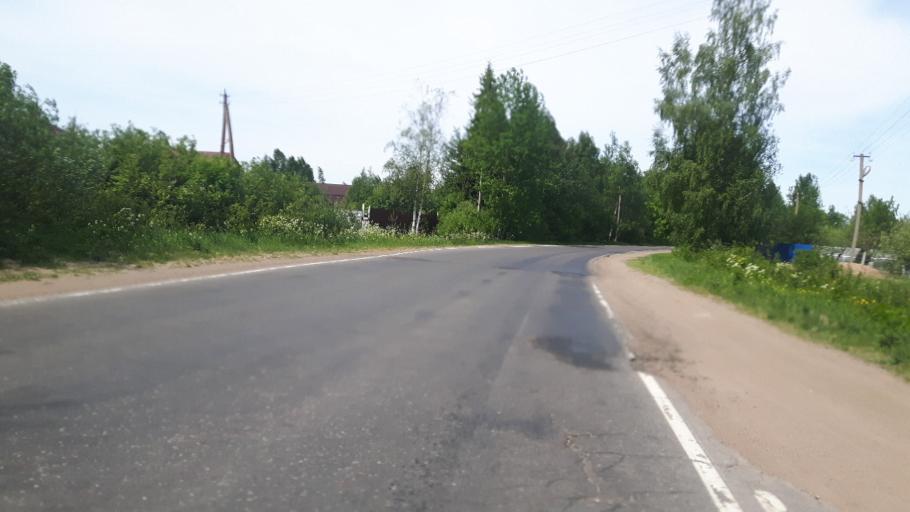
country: RU
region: Leningrad
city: Ust'-Luga
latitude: 59.6398
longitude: 28.2790
